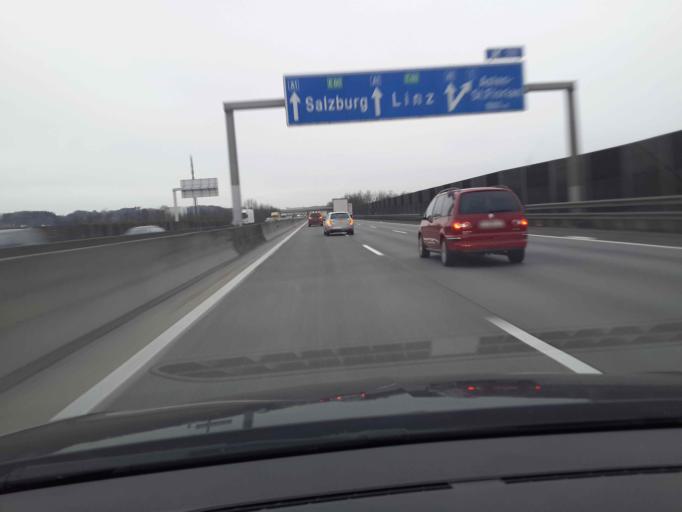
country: AT
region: Upper Austria
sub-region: Politischer Bezirk Linz-Land
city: Asten
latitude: 48.2119
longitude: 14.4248
